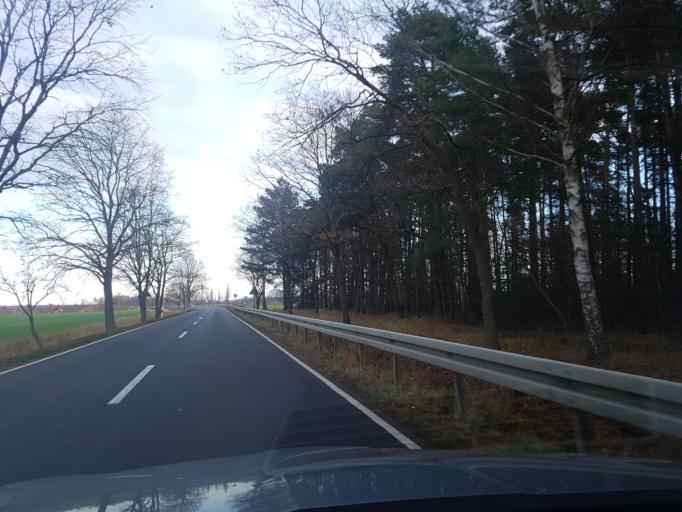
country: DE
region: Brandenburg
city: Golssen
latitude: 51.9920
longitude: 13.6607
